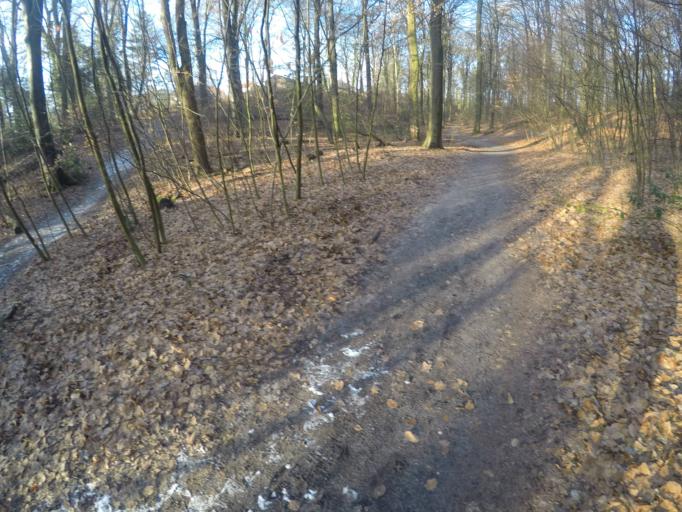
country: NL
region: Gelderland
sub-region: Gemeente Arnhem
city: Gulden Bodem
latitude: 51.9968
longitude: 5.8902
